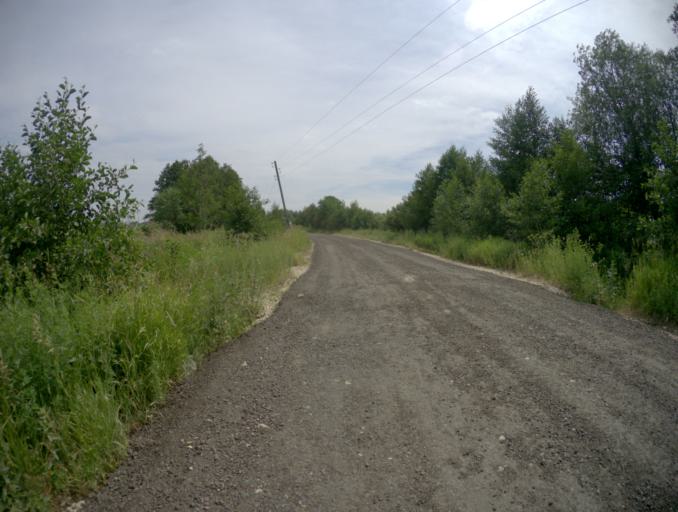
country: RU
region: Vladimir
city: Raduzhnyy
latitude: 56.0280
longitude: 40.2914
